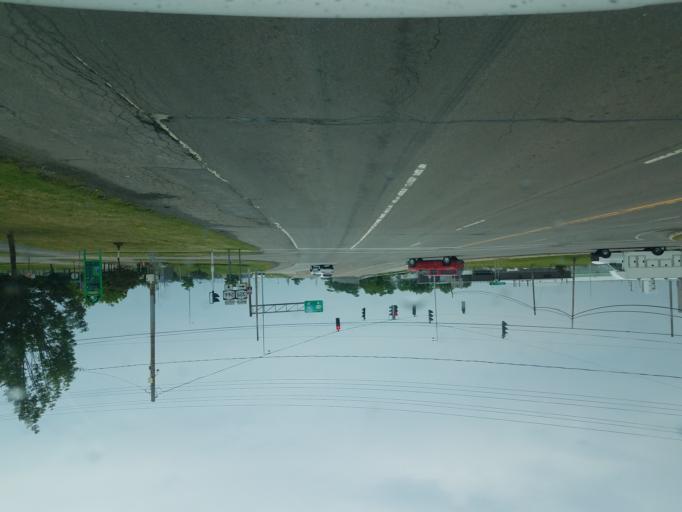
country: US
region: New York
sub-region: Erie County
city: Grandyle Village
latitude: 42.9662
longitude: -78.9230
